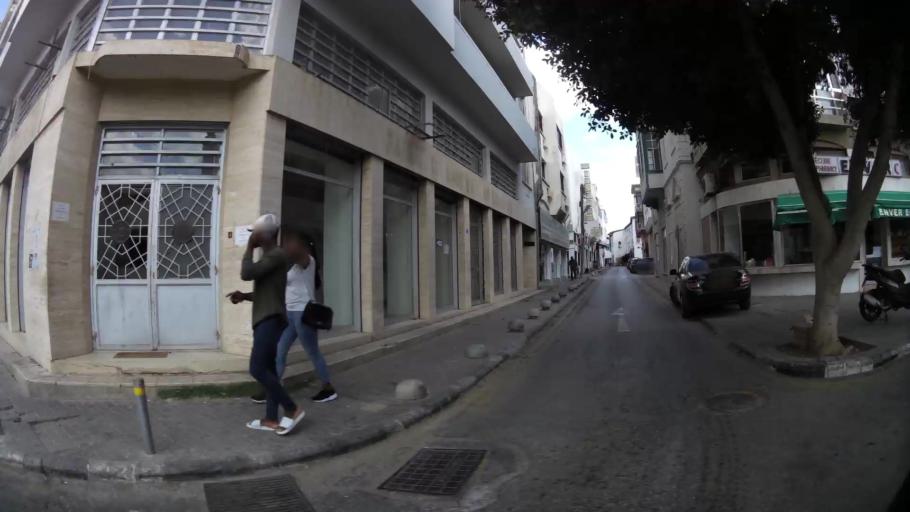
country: CY
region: Lefkosia
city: Nicosia
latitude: 35.1782
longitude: 33.3610
